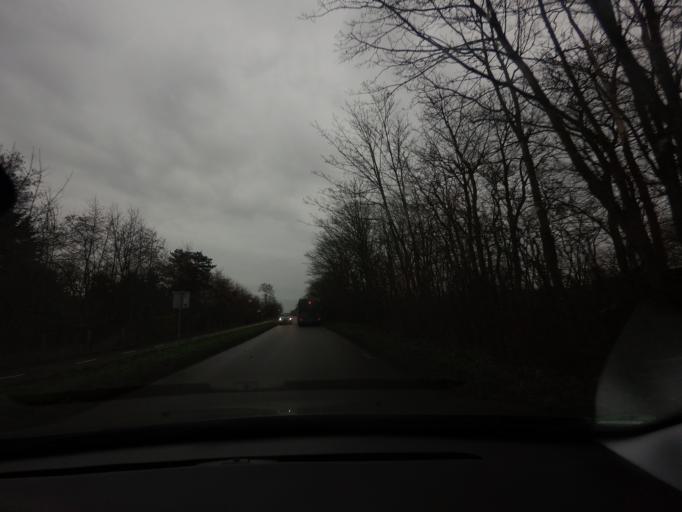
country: NL
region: North Holland
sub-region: Gemeente Texel
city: Den Burg
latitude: 53.0760
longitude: 4.7580
